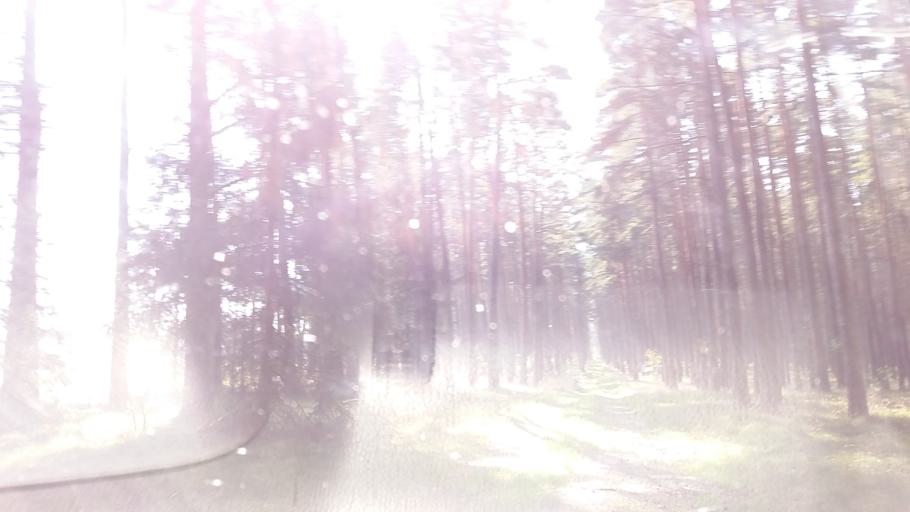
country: PL
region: West Pomeranian Voivodeship
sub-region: Powiat walecki
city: Tuczno
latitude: 53.2216
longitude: 16.0209
